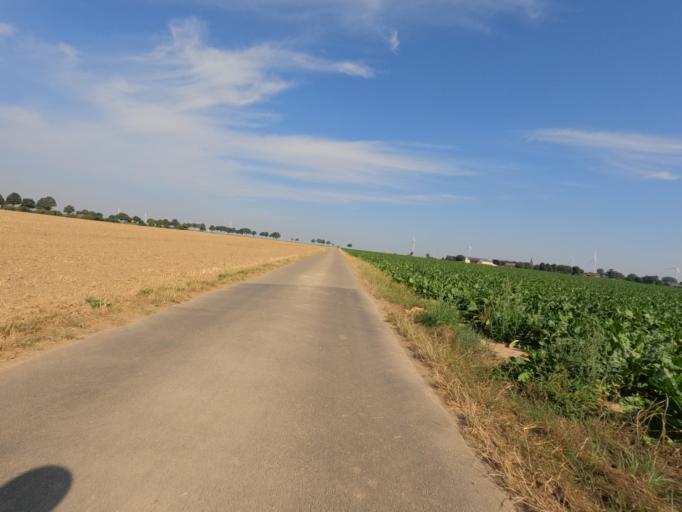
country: DE
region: North Rhine-Westphalia
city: Julich
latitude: 50.9910
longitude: 6.3432
